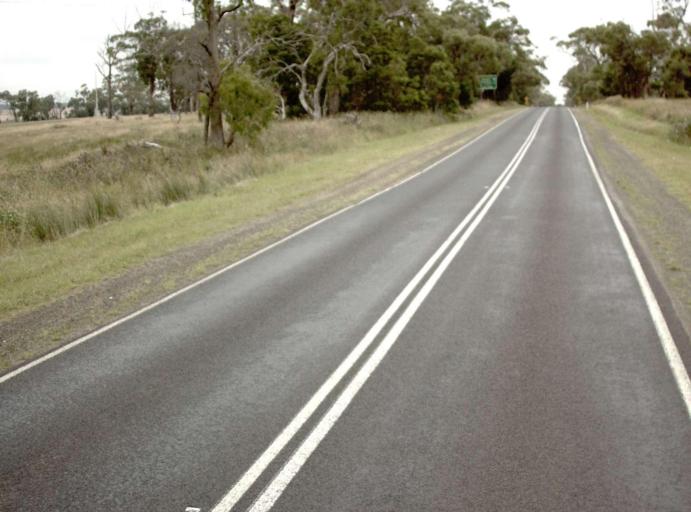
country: AU
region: Victoria
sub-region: Latrobe
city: Traralgon
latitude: -38.2402
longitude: 146.5060
